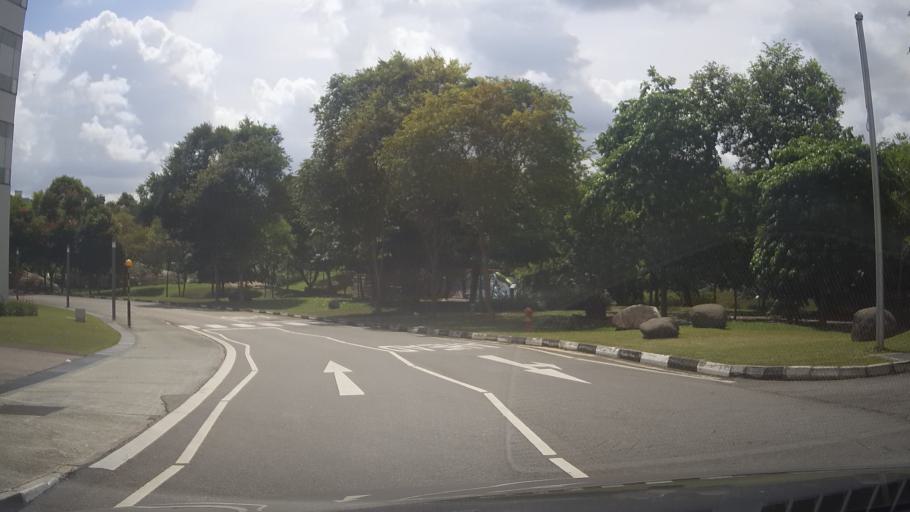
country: MY
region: Johor
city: Johor Bahru
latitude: 1.4440
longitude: 103.7842
